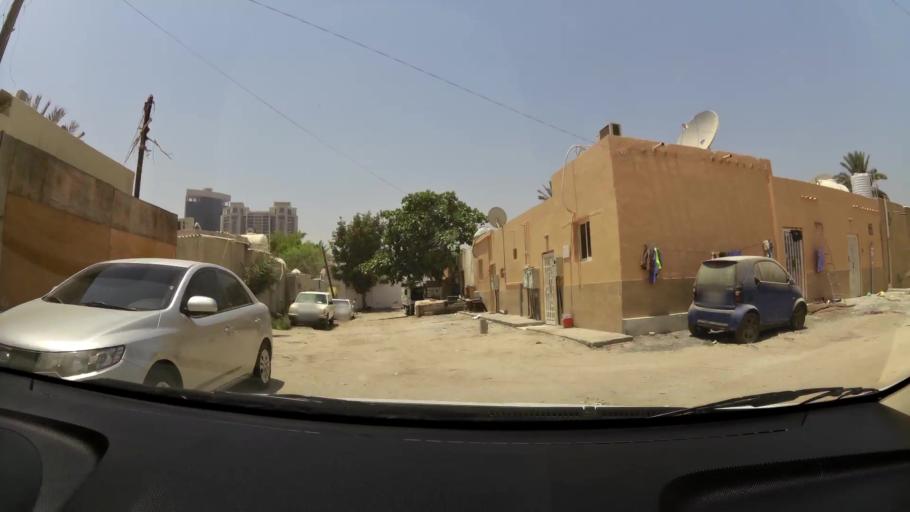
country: AE
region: Ajman
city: Ajman
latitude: 25.3975
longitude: 55.4398
